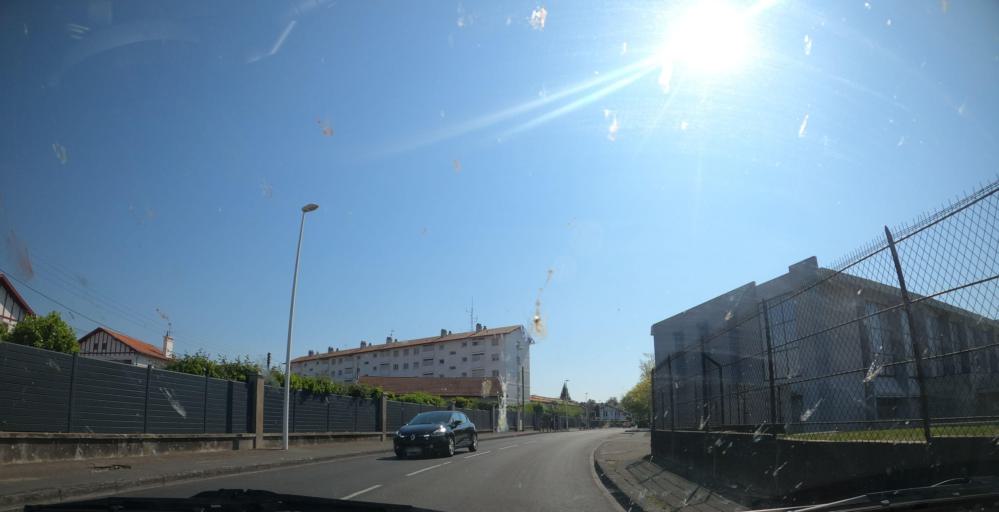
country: FR
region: Aquitaine
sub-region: Departement des Pyrenees-Atlantiques
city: Bayonne
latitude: 43.4775
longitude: -1.4818
